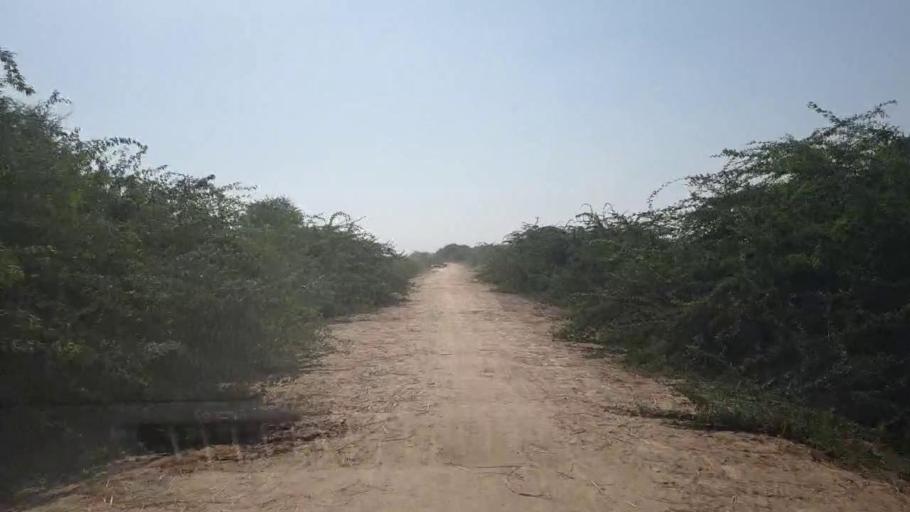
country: PK
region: Sindh
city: Talhar
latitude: 24.8224
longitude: 68.7939
